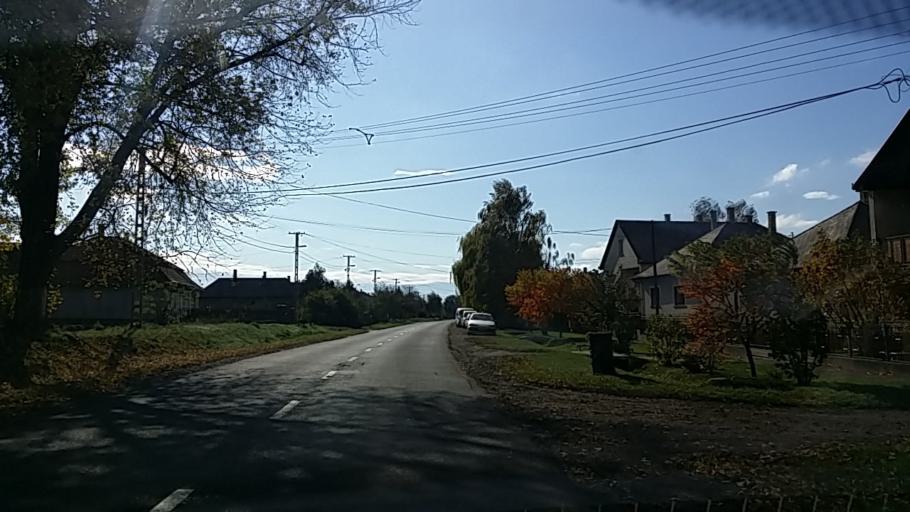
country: HU
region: Borsod-Abauj-Zemplen
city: Gonc
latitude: 48.4253
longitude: 21.2369
